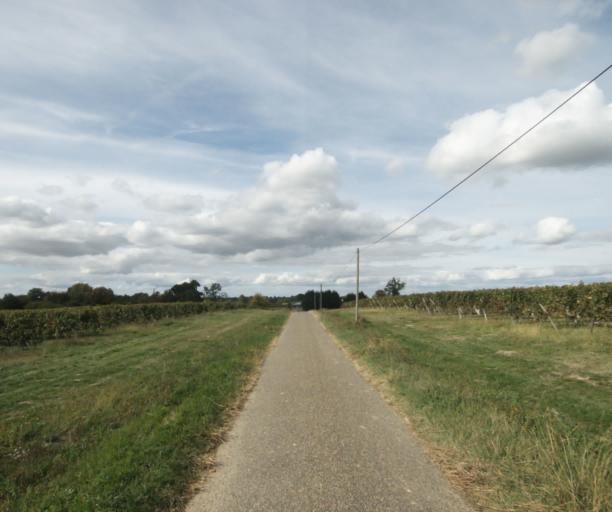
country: FR
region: Midi-Pyrenees
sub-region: Departement du Gers
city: Eauze
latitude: 43.8499
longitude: 0.1535
